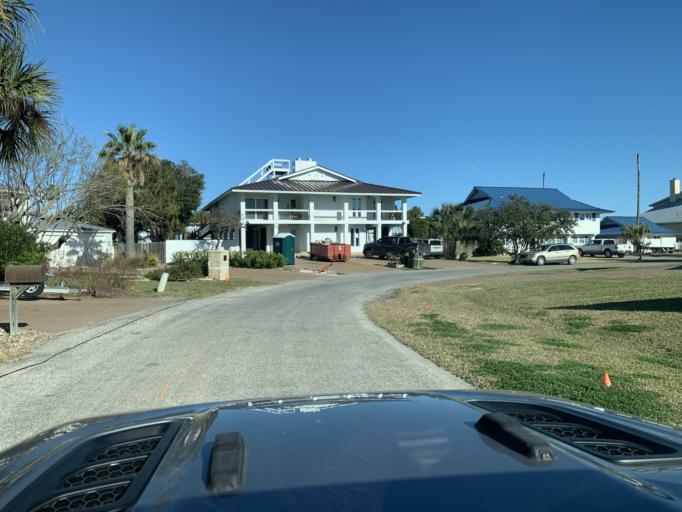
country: US
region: Texas
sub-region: Aransas County
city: Fulton
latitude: 28.0388
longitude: -97.0307
